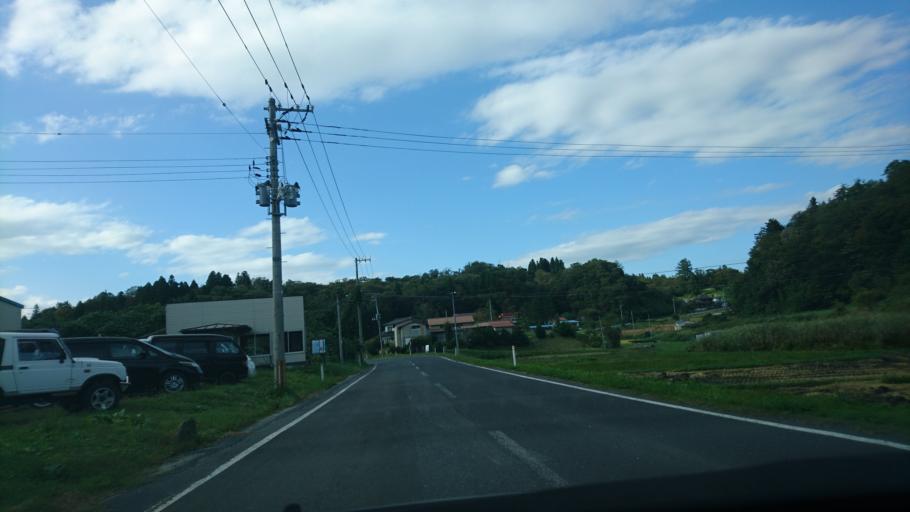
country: JP
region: Iwate
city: Ichinoseki
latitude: 38.8712
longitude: 141.3484
